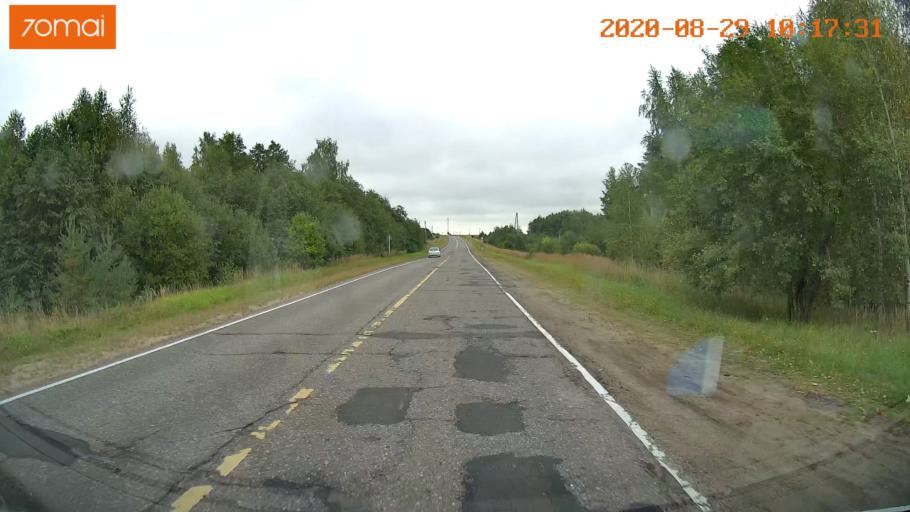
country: RU
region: Ivanovo
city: Yur'yevets
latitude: 57.3340
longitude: 42.8147
